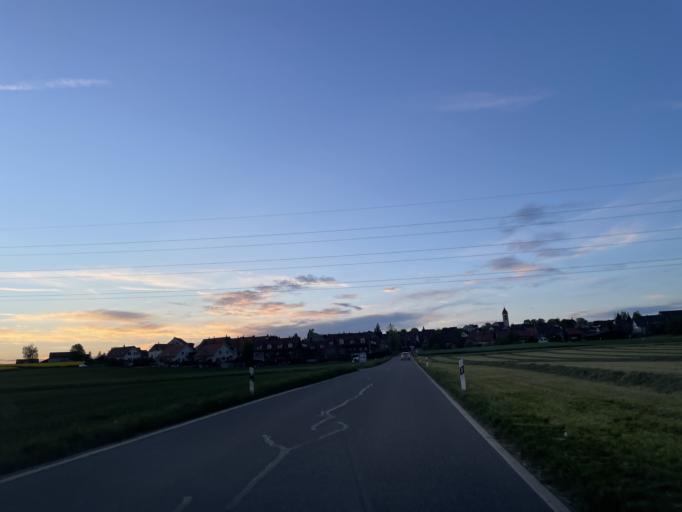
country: CH
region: Zurich
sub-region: Bezirk Winterthur
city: Brutten
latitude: 47.4677
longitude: 8.6753
